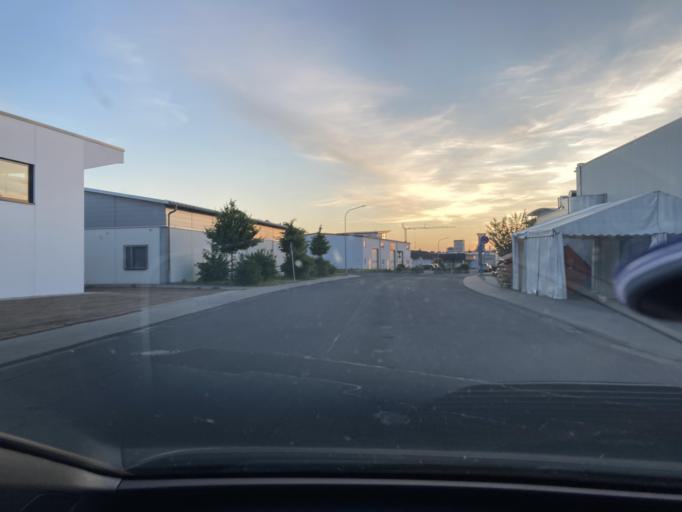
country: DE
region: Hesse
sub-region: Regierungsbezirk Darmstadt
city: Eppertshausen
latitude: 49.9685
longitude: 8.8277
